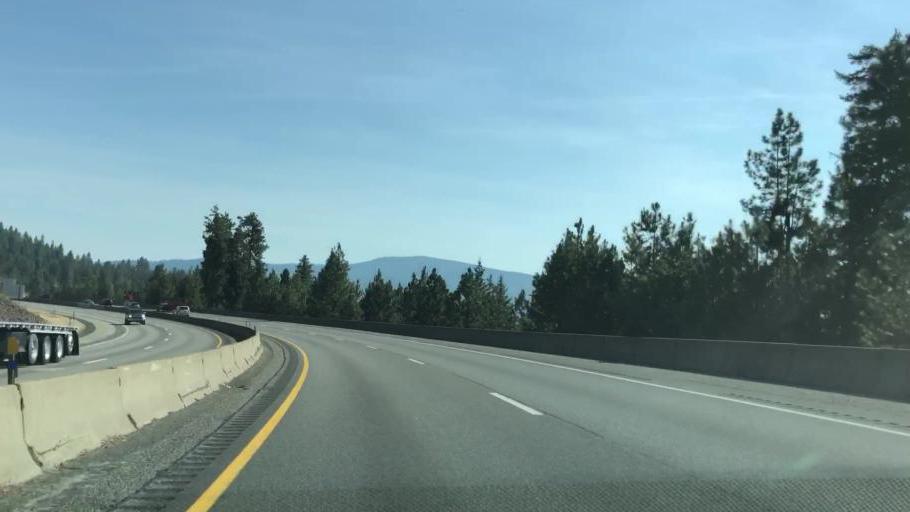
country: US
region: Idaho
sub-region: Kootenai County
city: Coeur d'Alene
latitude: 47.6422
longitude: -116.7131
